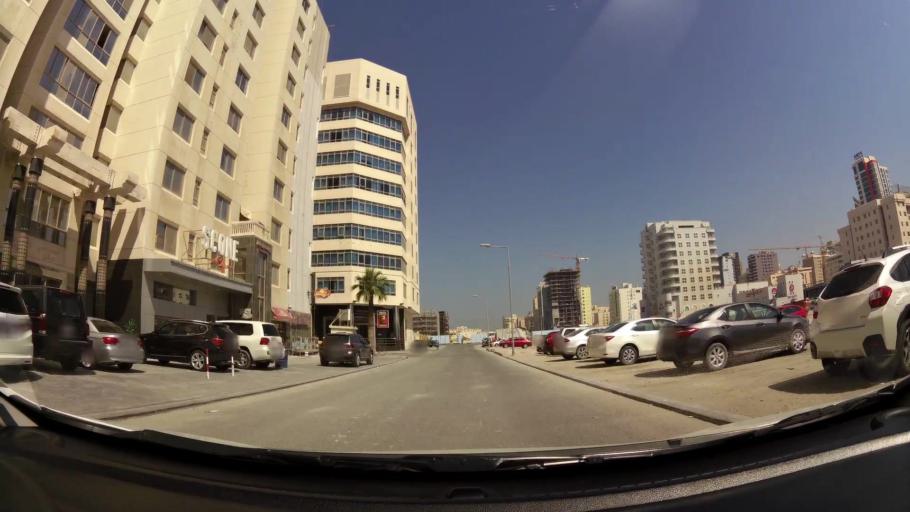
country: BH
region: Manama
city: Manama
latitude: 26.2143
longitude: 50.6003
